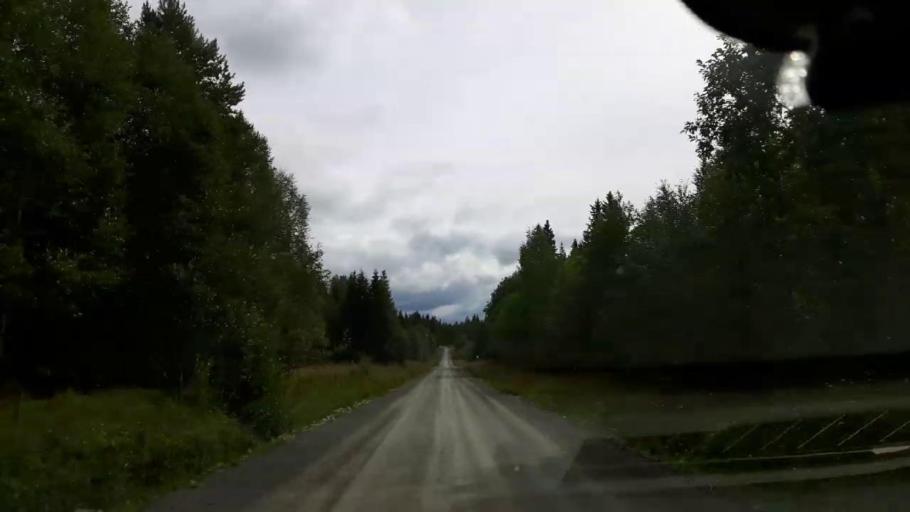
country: SE
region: Jaemtland
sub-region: Krokoms Kommun
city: Valla
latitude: 63.6441
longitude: 13.9916
